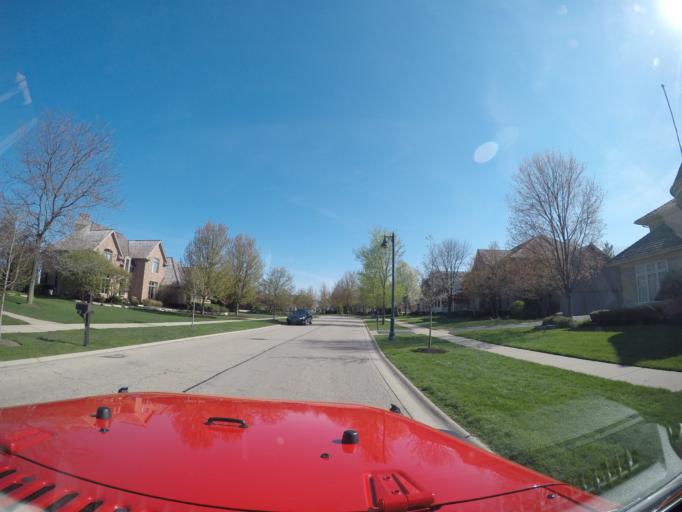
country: US
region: Illinois
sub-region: Cook County
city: Northbrook
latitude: 42.0853
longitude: -87.8330
